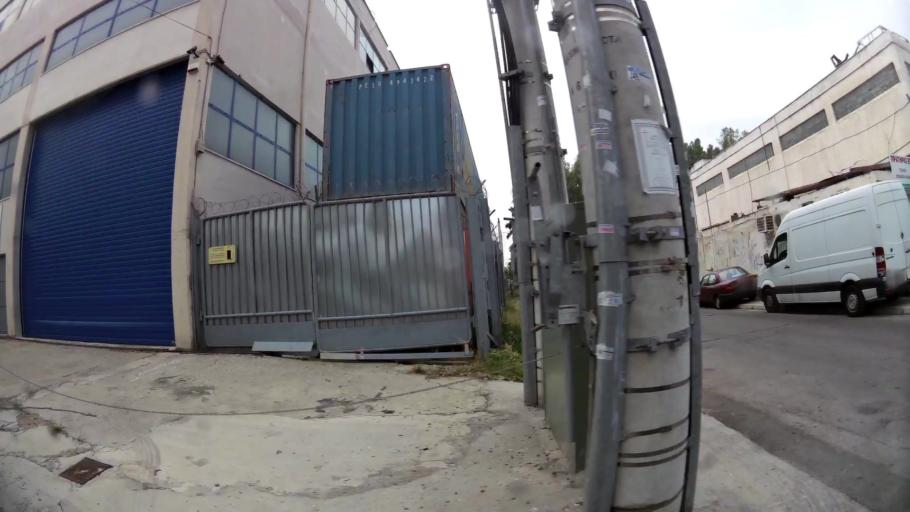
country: GR
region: Attica
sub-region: Nomos Piraios
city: Agios Ioannis Rentis
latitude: 37.9621
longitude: 23.6641
